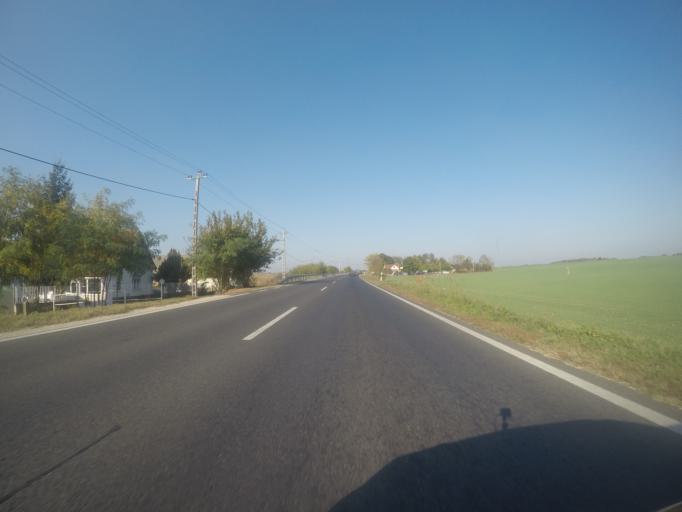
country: HU
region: Tolna
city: Dunafoldvar
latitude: 46.8413
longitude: 18.9101
